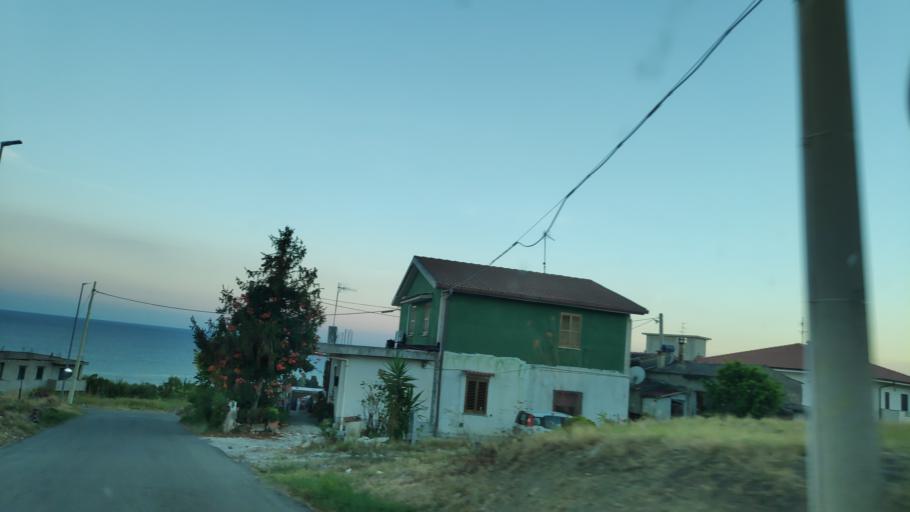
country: IT
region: Calabria
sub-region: Provincia di Reggio Calabria
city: Riace Marina
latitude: 38.3918
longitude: 16.5279
